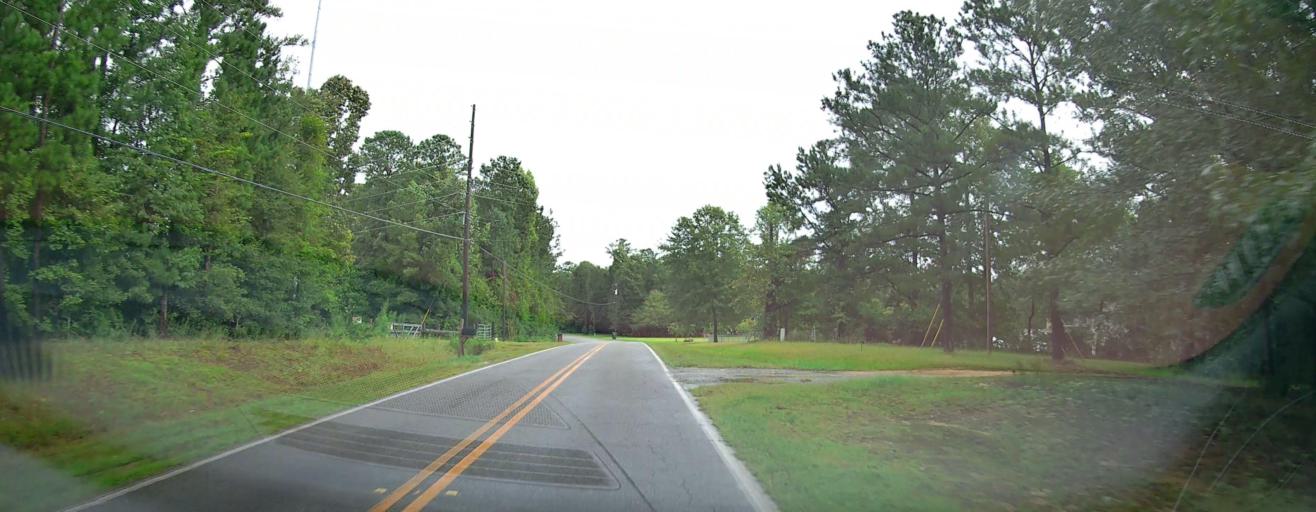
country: US
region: Georgia
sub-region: Bibb County
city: West Point
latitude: 32.8025
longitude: -83.8257
